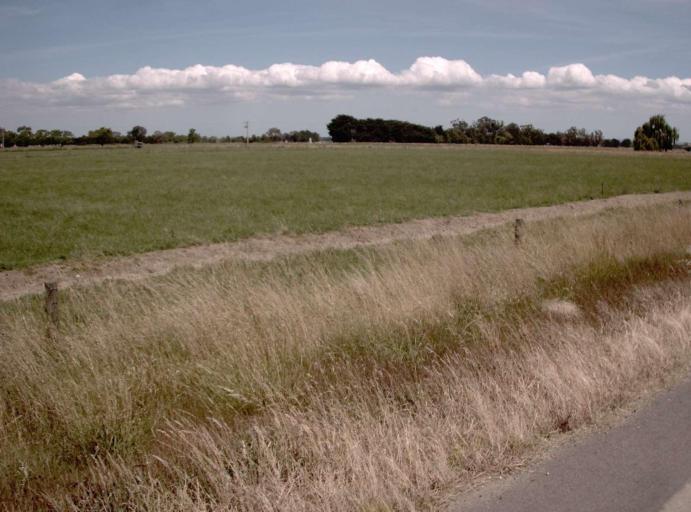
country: AU
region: Victoria
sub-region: Wellington
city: Heyfield
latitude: -38.0243
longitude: 146.8806
